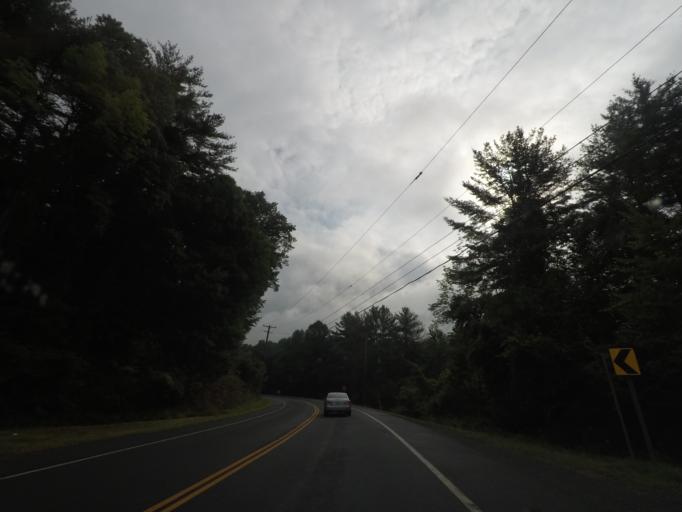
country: US
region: New York
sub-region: Rensselaer County
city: Nassau
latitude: 42.4953
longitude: -73.5344
